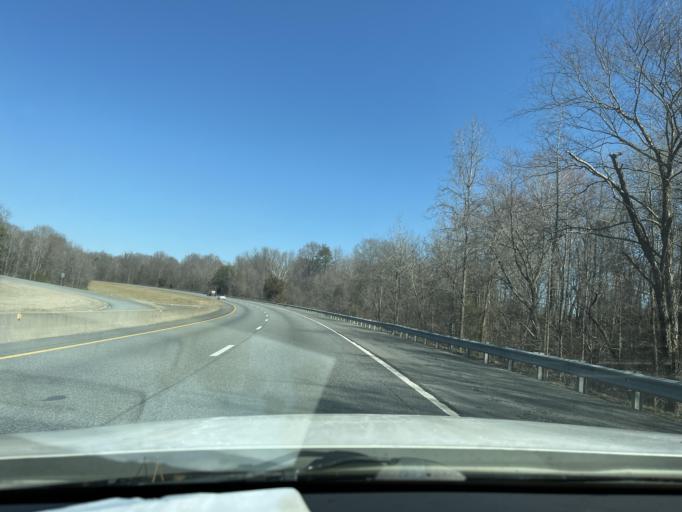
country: US
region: North Carolina
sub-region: Guilford County
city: Jamestown
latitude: 35.9853
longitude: -79.8812
